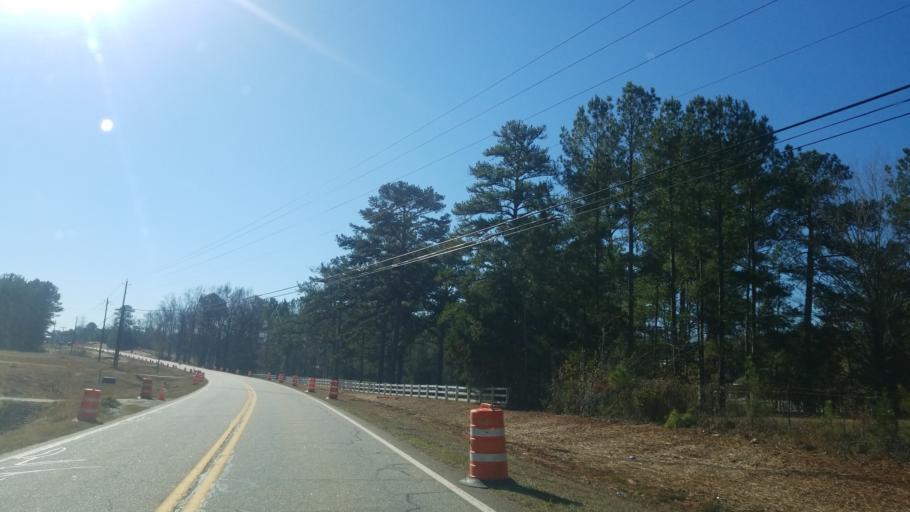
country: US
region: Alabama
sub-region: Lee County
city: Smiths Station
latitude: 32.6613
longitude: -85.0601
